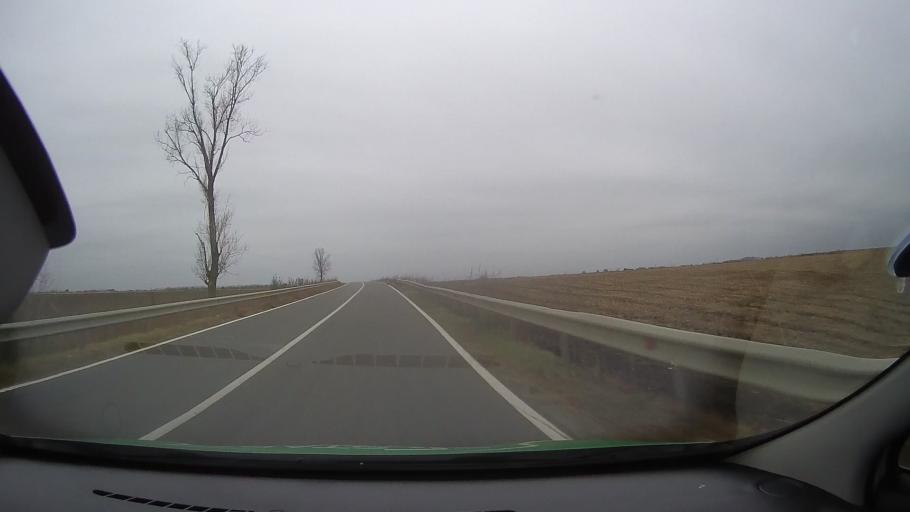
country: RO
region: Ialomita
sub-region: Comuna Slobozia
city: Slobozia
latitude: 44.6186
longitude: 27.3882
